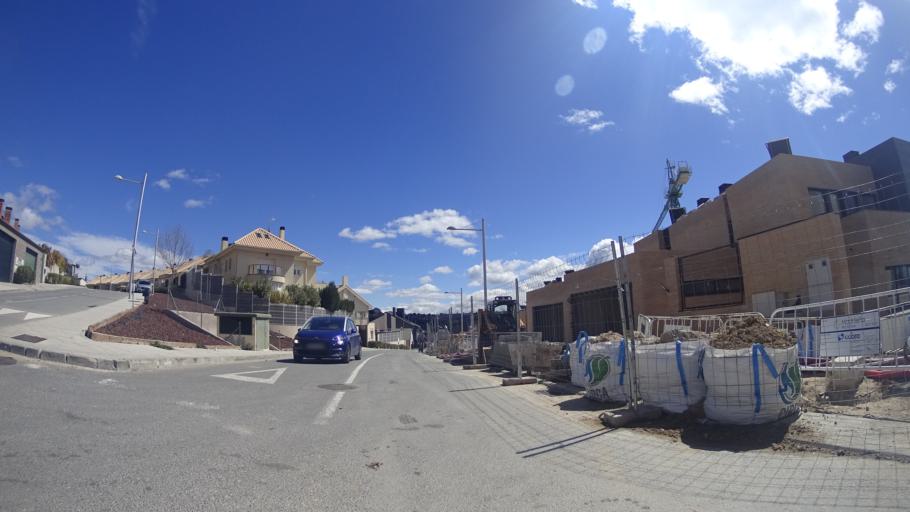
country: ES
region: Madrid
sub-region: Provincia de Madrid
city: Torrelodones
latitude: 40.5639
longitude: -3.9206
